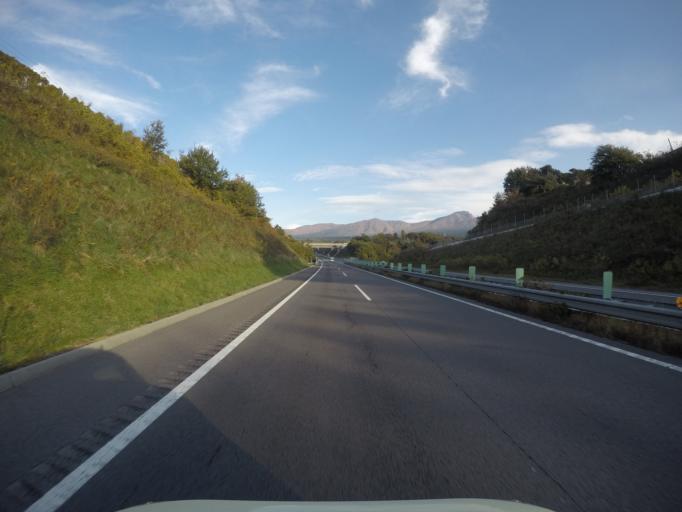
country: JP
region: Nagano
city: Komoro
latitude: 36.3155
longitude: 138.4791
